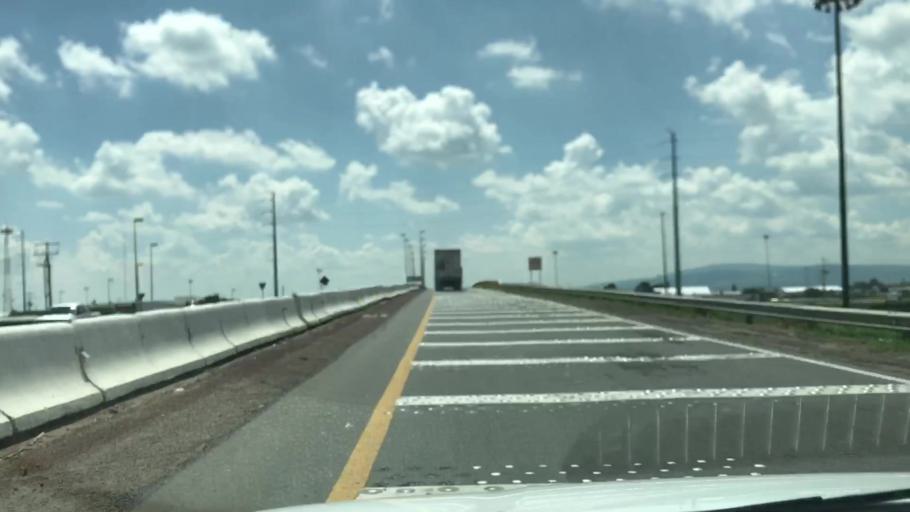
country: MX
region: Guanajuato
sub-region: Irapuato
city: Las Huertas Tercera Seccion
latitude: 20.6496
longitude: -101.3721
